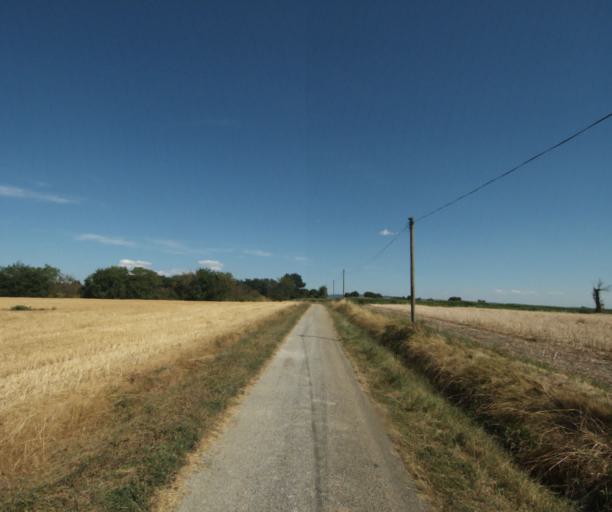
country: FR
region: Midi-Pyrenees
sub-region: Departement de la Haute-Garonne
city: Saint-Felix-Lauragais
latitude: 43.5065
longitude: 1.9084
